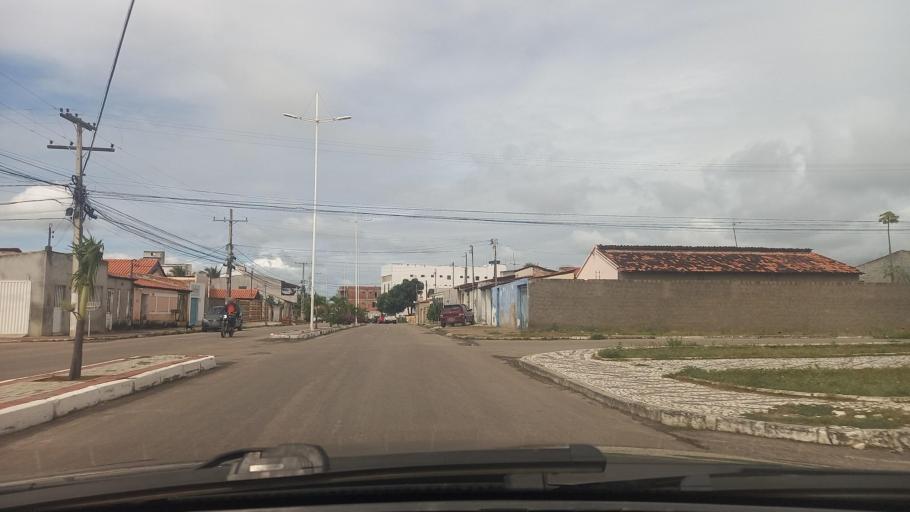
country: BR
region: Bahia
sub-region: Paulo Afonso
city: Paulo Afonso
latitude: -9.4382
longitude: -38.2090
